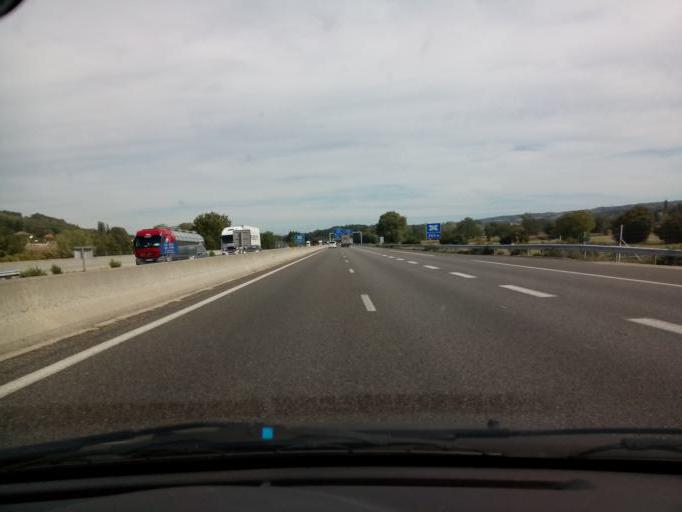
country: FR
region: Rhone-Alpes
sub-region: Departement de l'Isere
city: Ruy
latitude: 45.5703
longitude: 5.3348
